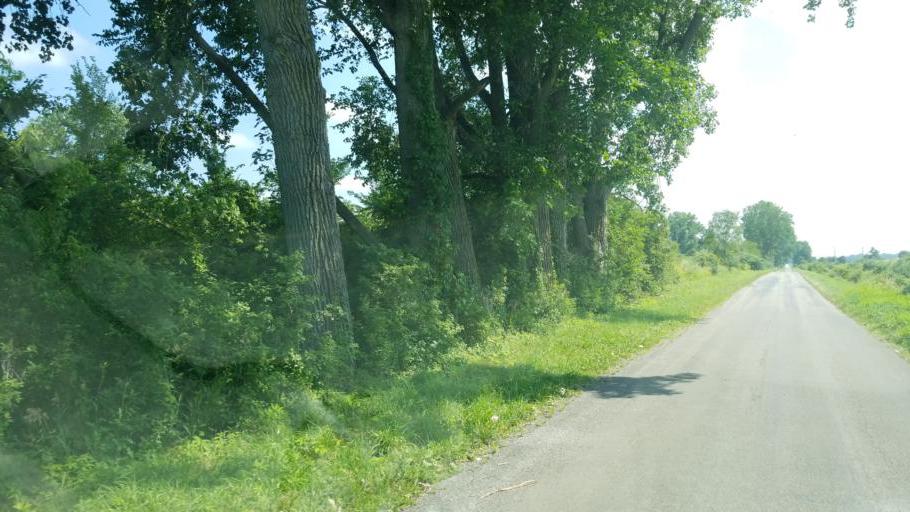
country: US
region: Ohio
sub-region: Huron County
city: Willard
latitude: 41.0132
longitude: -82.7809
